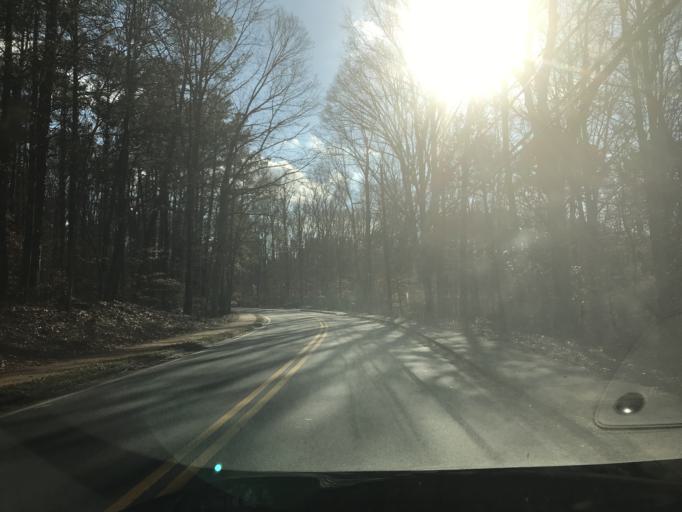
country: US
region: Georgia
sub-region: Fulton County
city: College Park
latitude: 33.6488
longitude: -84.4724
